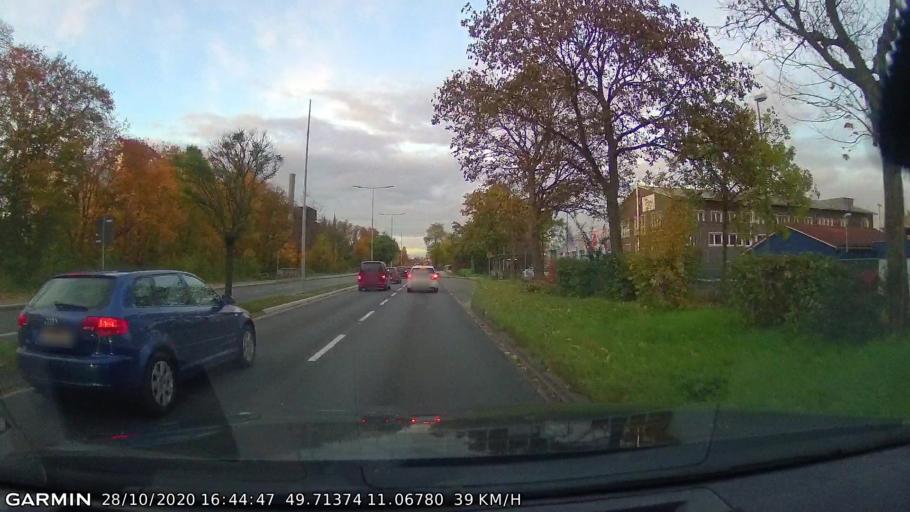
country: DE
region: Bavaria
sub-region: Upper Franconia
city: Forchheim
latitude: 49.7138
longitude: 11.0678
